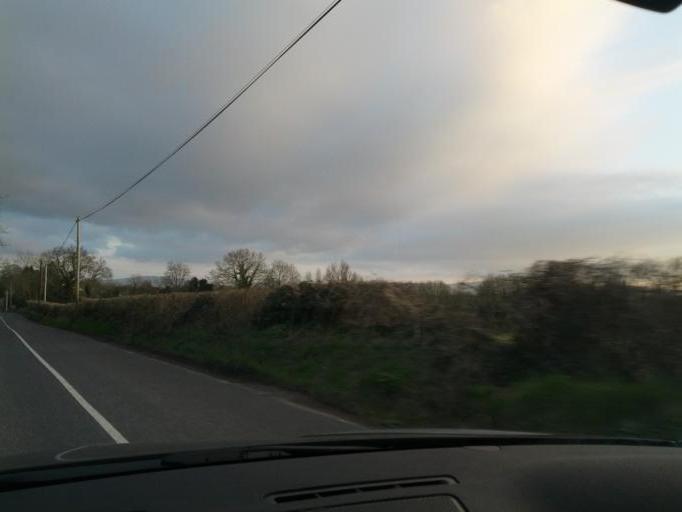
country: IE
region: Munster
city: Nenagh Bridge
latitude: 52.8956
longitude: -8.2048
